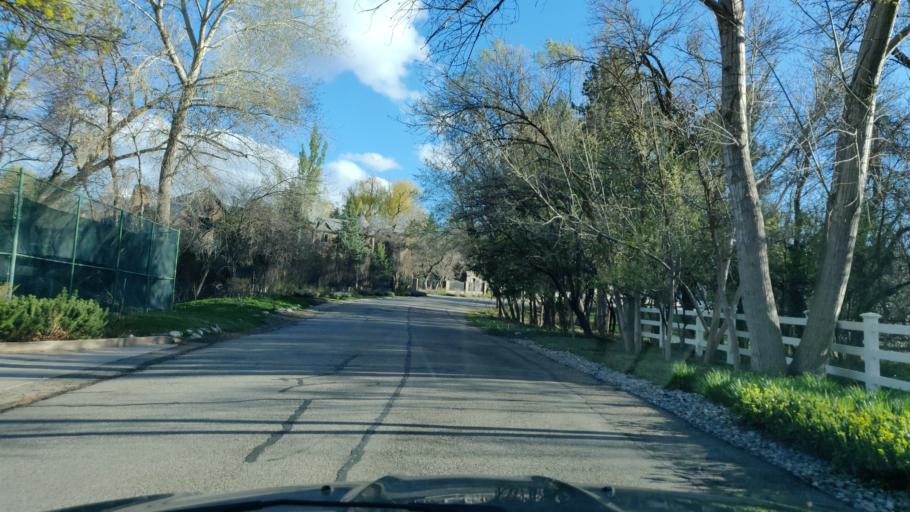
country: US
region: Utah
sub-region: Salt Lake County
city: Holladay
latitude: 40.6437
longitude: -111.8218
